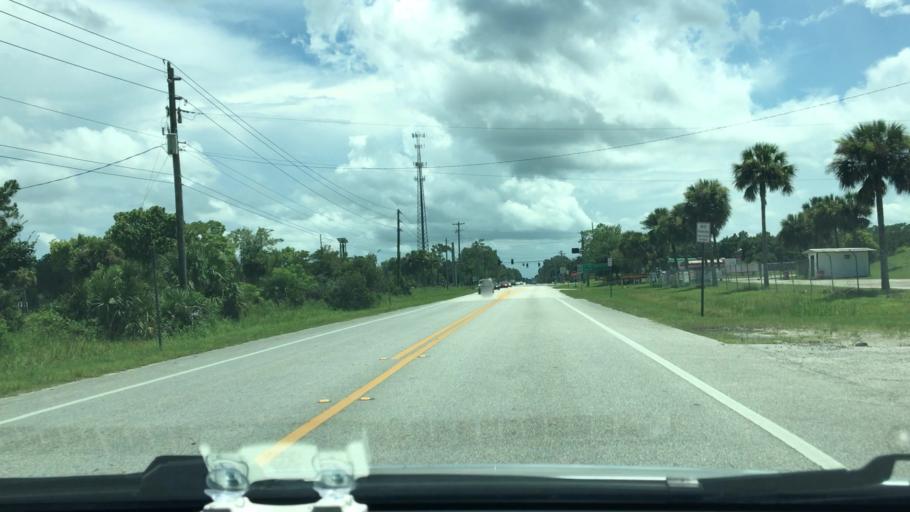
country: US
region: Florida
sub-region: Volusia County
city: Samsula-Spruce Creek
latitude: 29.0134
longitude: -81.0686
